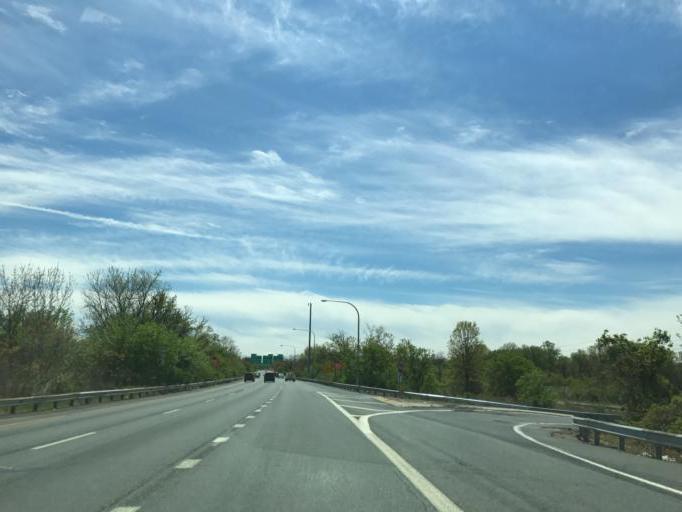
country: US
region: Delaware
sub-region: New Castle County
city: Newport
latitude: 39.7077
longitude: -75.6076
